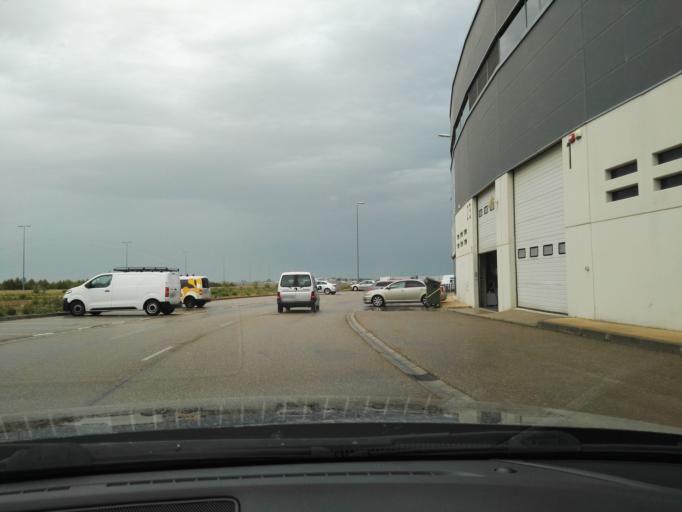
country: ES
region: Aragon
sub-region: Provincia de Zaragoza
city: Montecanal
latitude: 41.6481
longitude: -0.9961
